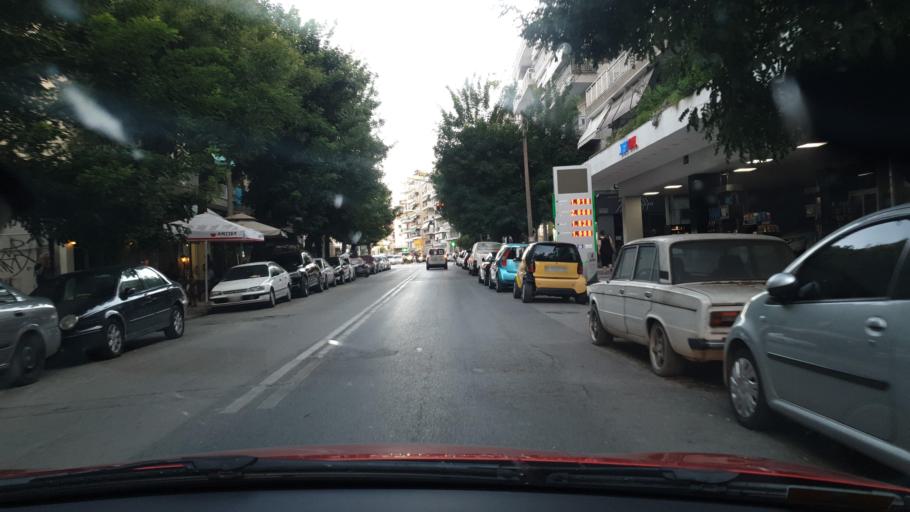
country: GR
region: Central Macedonia
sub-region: Nomos Thessalonikis
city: Triandria
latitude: 40.6078
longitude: 22.9577
